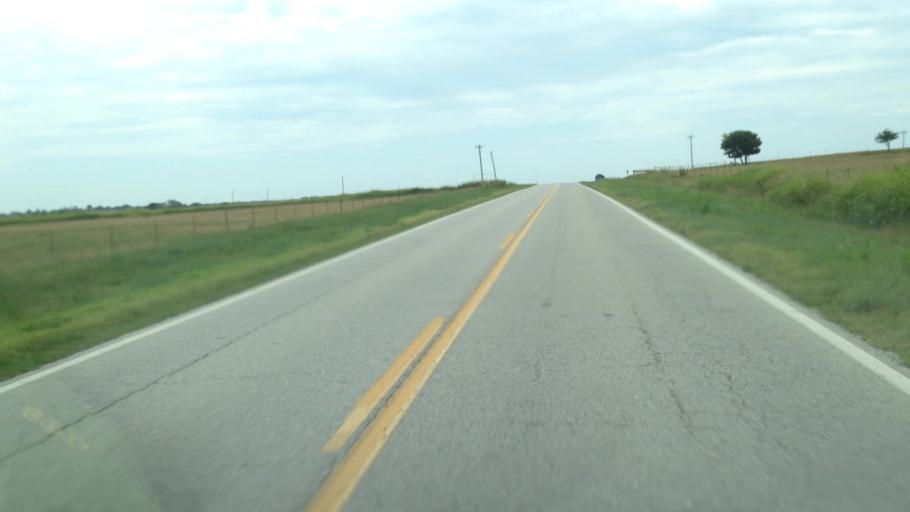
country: US
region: Kansas
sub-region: Labette County
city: Chetopa
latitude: 36.8429
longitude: -95.1269
